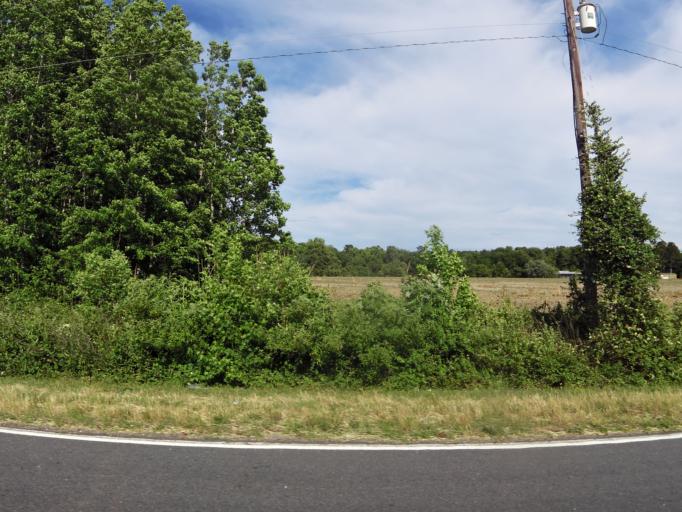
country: US
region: South Carolina
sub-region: Allendale County
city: Fairfax
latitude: 33.0311
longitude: -81.2232
